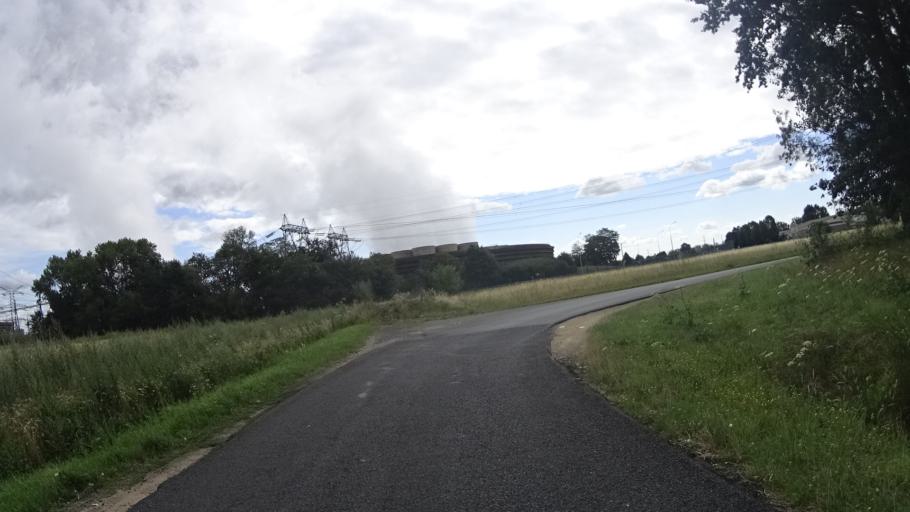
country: FR
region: Centre
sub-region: Departement d'Indre-et-Loire
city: Savigny-en-Veron
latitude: 47.2227
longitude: 0.1607
